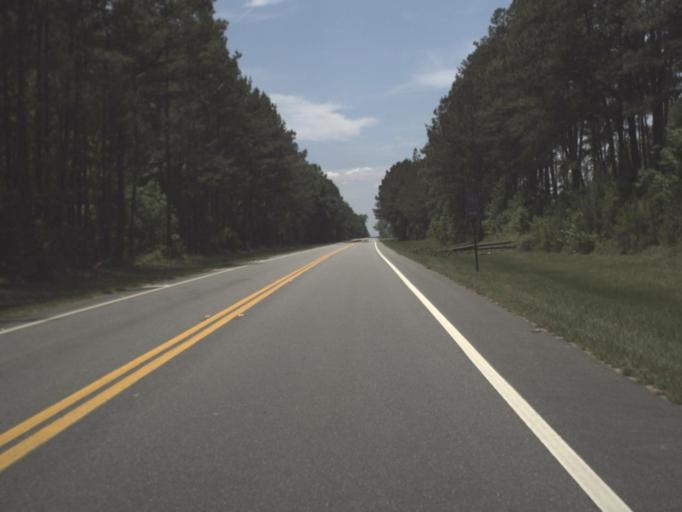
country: US
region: Florida
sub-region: Gulf County
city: Wewahitchka
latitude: 30.2855
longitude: -85.1469
